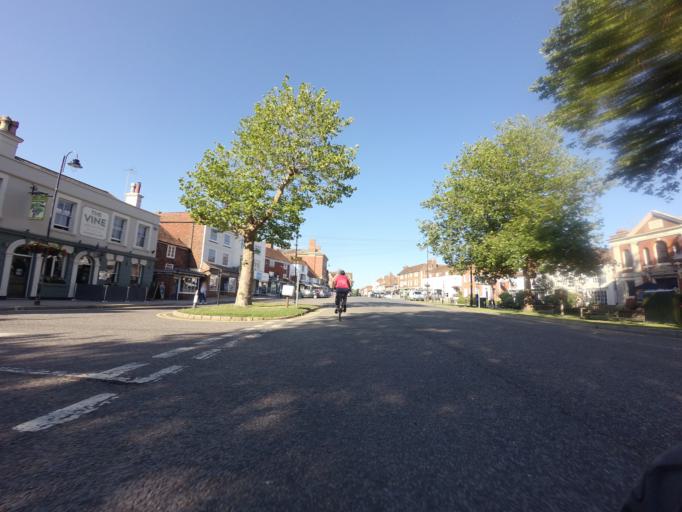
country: GB
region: England
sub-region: Kent
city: Tenterden
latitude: 51.0677
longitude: 0.6855
